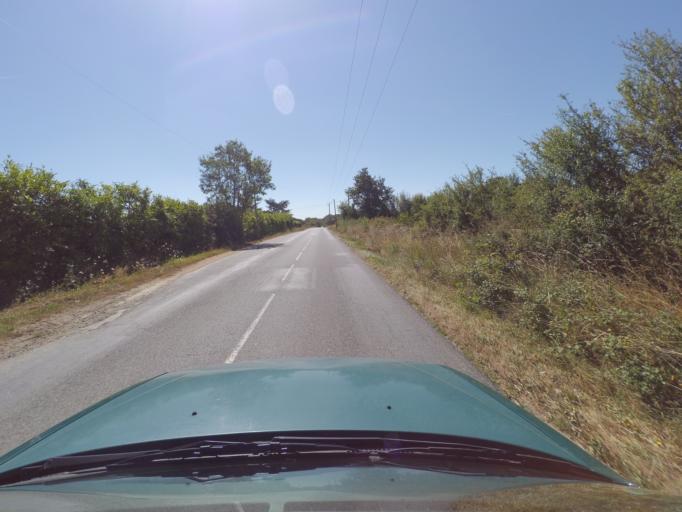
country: FR
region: Pays de la Loire
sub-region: Departement de la Loire-Atlantique
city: Les Sorinieres
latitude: 47.1291
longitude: -1.5149
